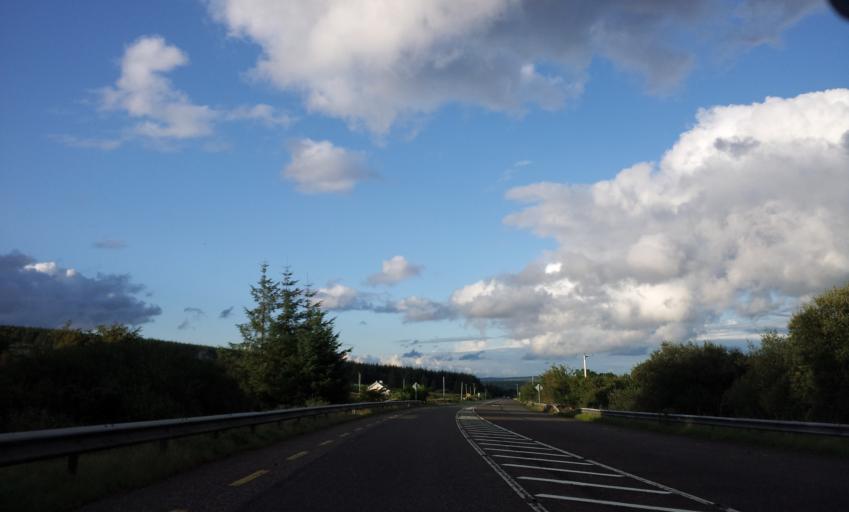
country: IE
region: Munster
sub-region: Ciarrai
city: Castleisland
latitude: 52.2743
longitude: -9.4156
